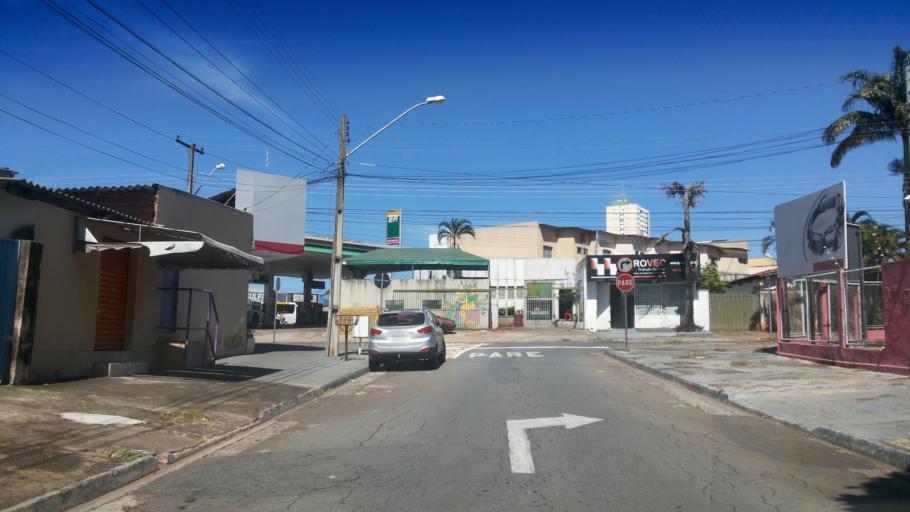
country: BR
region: Goias
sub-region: Goiania
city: Goiania
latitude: -16.7197
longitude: -49.2594
